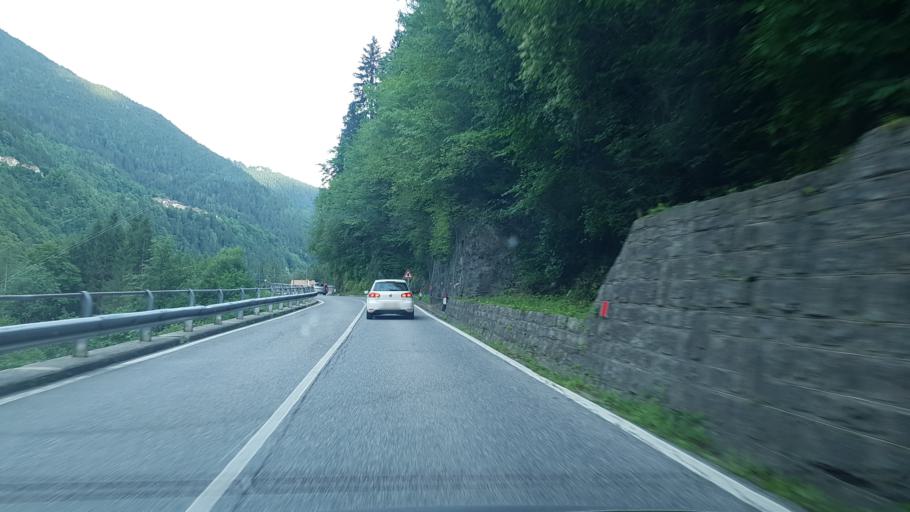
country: IT
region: Friuli Venezia Giulia
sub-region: Provincia di Udine
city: Rigolato
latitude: 46.5600
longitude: 12.8457
